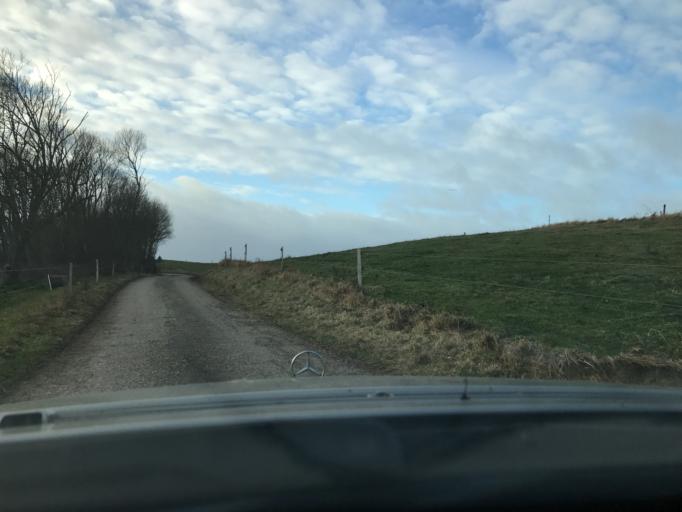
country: DK
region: South Denmark
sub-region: Sonderborg Kommune
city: Nordborg
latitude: 55.0523
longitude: 9.6429
